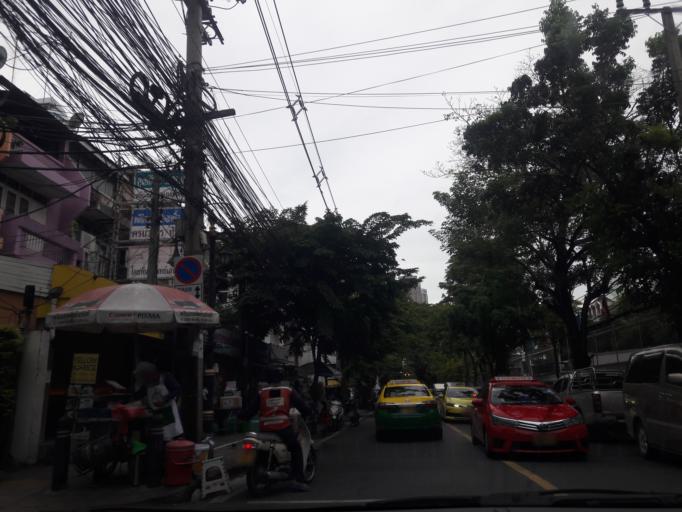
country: TH
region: Bangkok
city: Bang Rak
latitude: 13.7251
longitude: 100.5345
